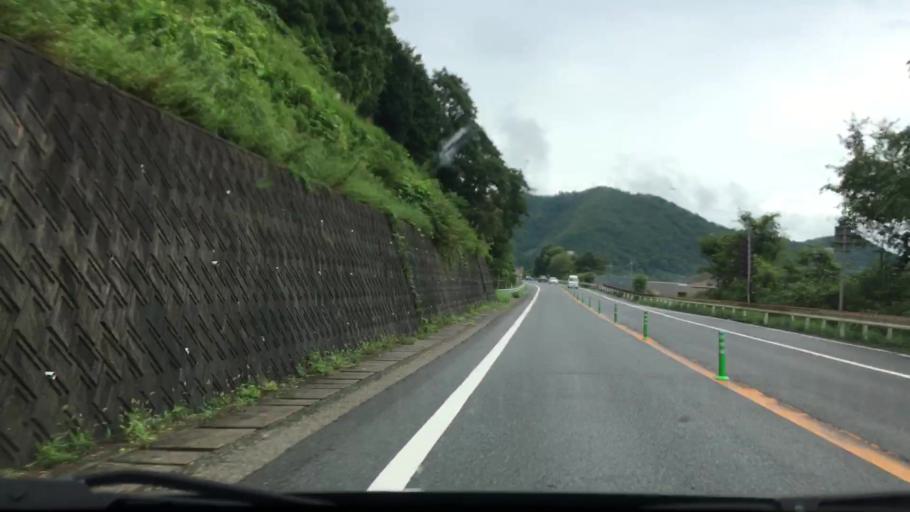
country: JP
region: Hyogo
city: Himeji
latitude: 35.0105
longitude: 134.7618
